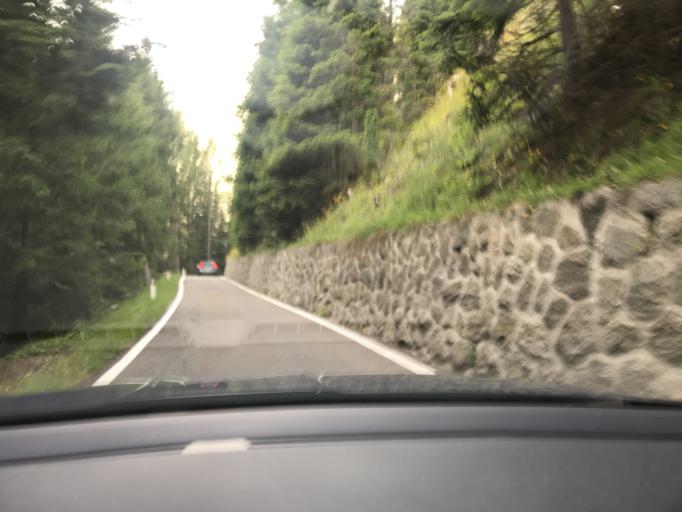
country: IT
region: Trentino-Alto Adige
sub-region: Bolzano
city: San Martino
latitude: 46.8906
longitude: 12.1923
